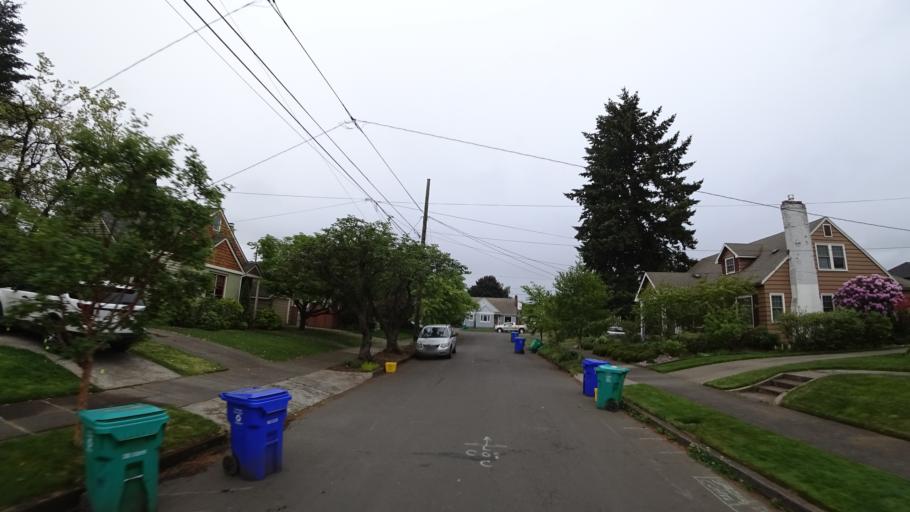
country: US
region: Oregon
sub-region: Multnomah County
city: Portland
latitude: 45.5509
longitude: -122.6245
